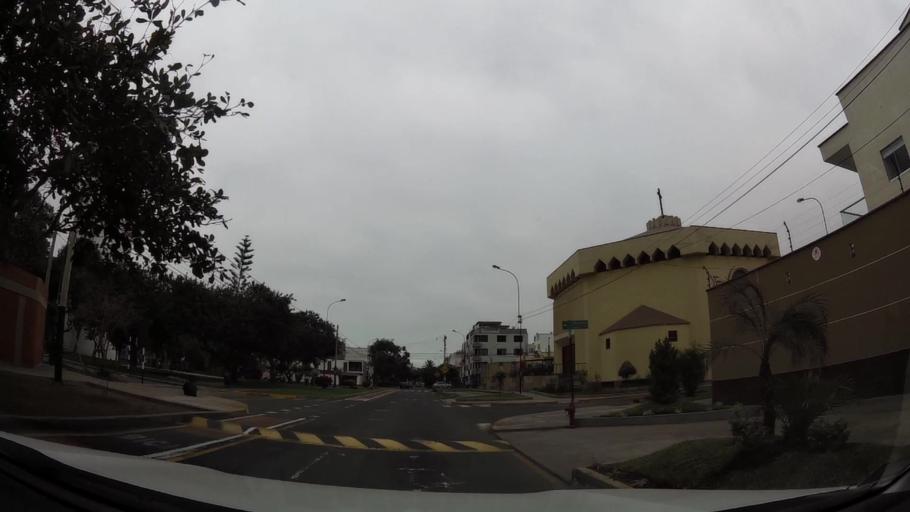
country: PE
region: Lima
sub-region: Lima
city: Surco
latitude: -12.1320
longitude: -76.9908
